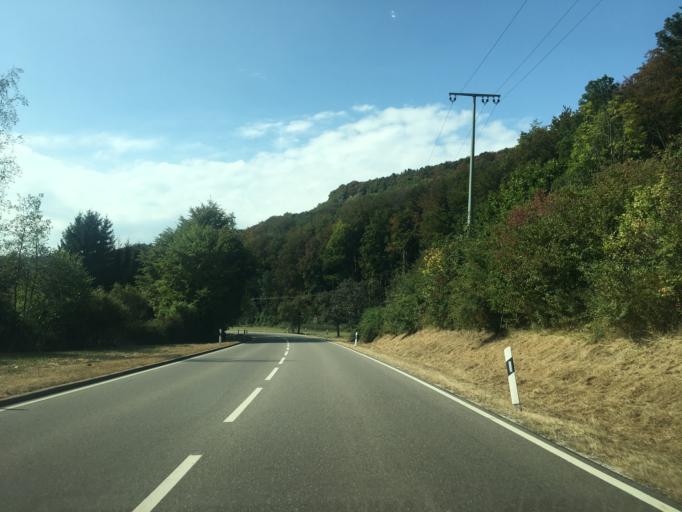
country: DE
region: Baden-Wuerttemberg
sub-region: Tuebingen Region
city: Pfullingen
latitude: 48.4301
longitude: 9.1741
